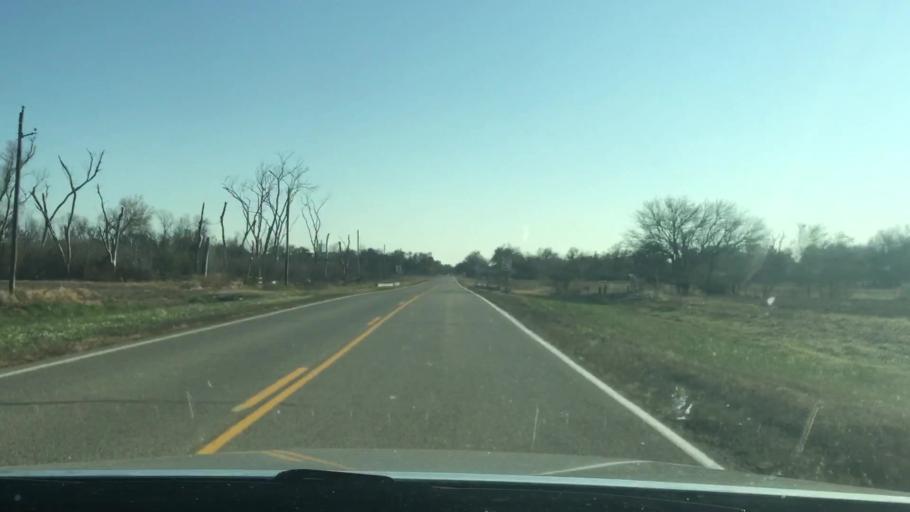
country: US
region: Kansas
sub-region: Reno County
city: Nickerson
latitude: 38.1617
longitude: -98.0875
